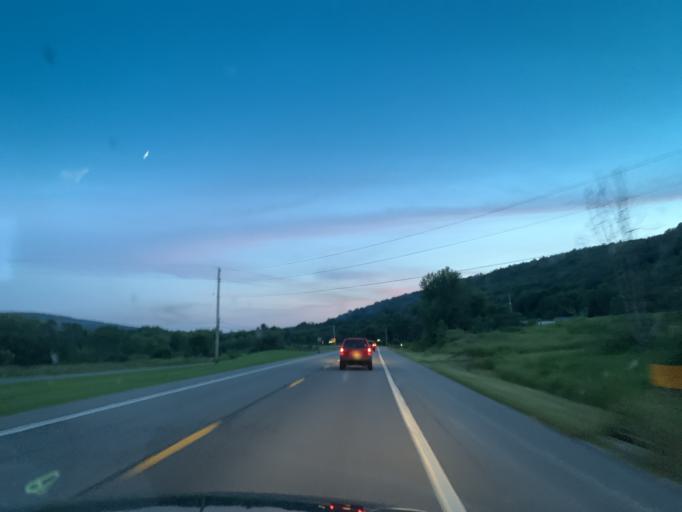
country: US
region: New York
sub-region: Chenango County
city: New Berlin
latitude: 42.5572
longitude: -75.3631
